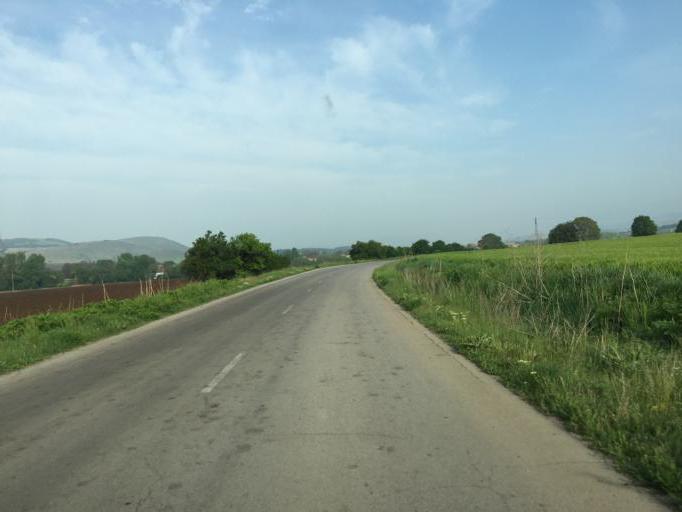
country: BG
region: Kyustendil
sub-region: Obshtina Bobovdol
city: Bobovdol
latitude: 42.4680
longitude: 23.0759
